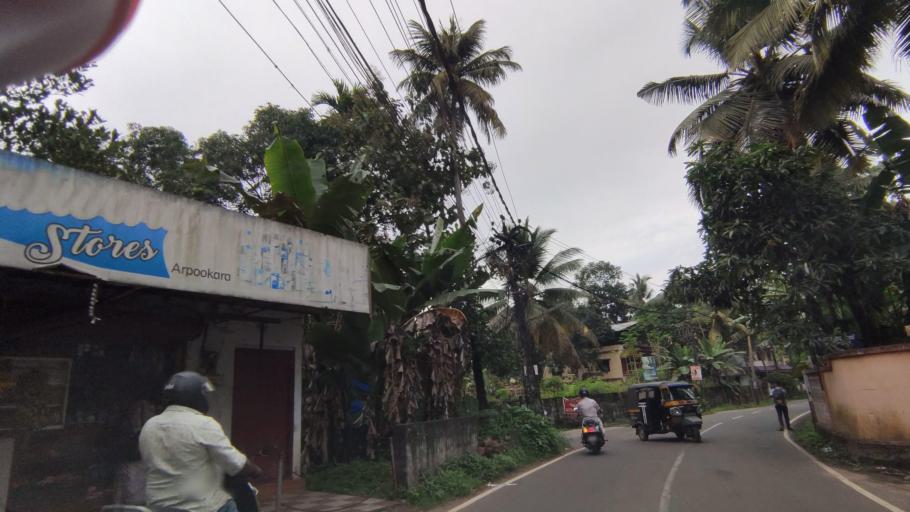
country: IN
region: Kerala
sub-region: Kottayam
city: Kottayam
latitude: 9.6334
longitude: 76.5144
